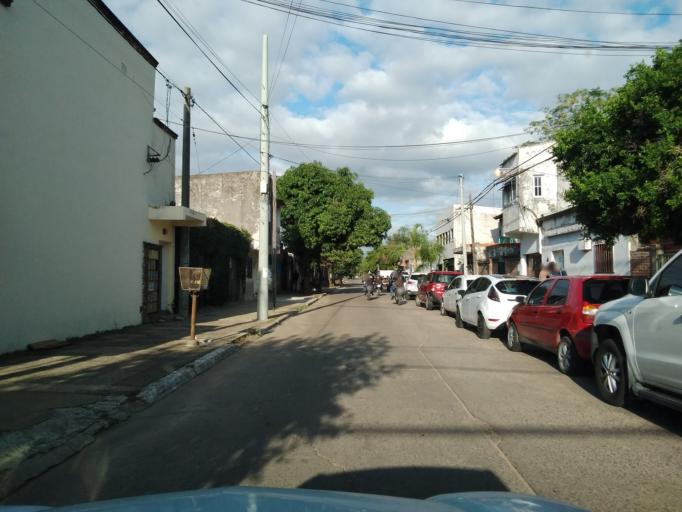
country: AR
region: Corrientes
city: Corrientes
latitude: -27.4656
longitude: -58.8205
